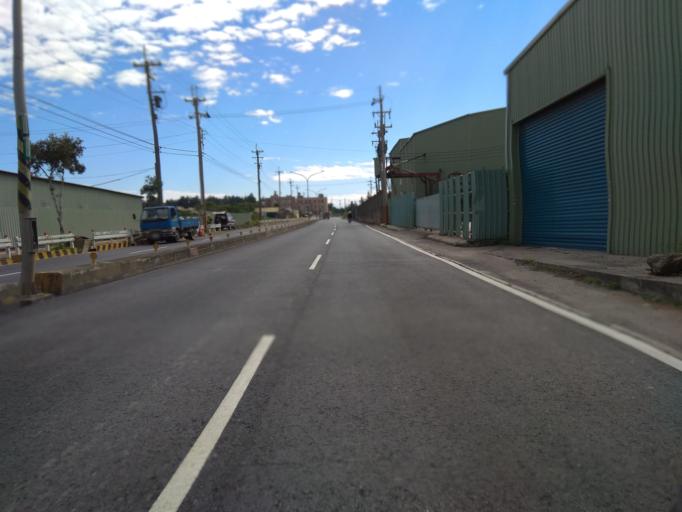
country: TW
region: Taiwan
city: Taoyuan City
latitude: 25.0612
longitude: 121.1341
